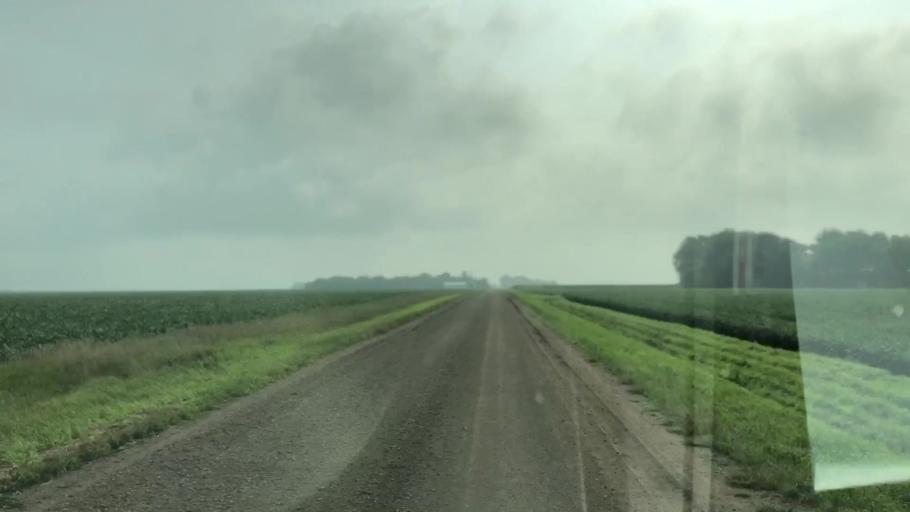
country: US
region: Iowa
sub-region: Sioux County
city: Hull
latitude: 43.2298
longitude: -96.0483
